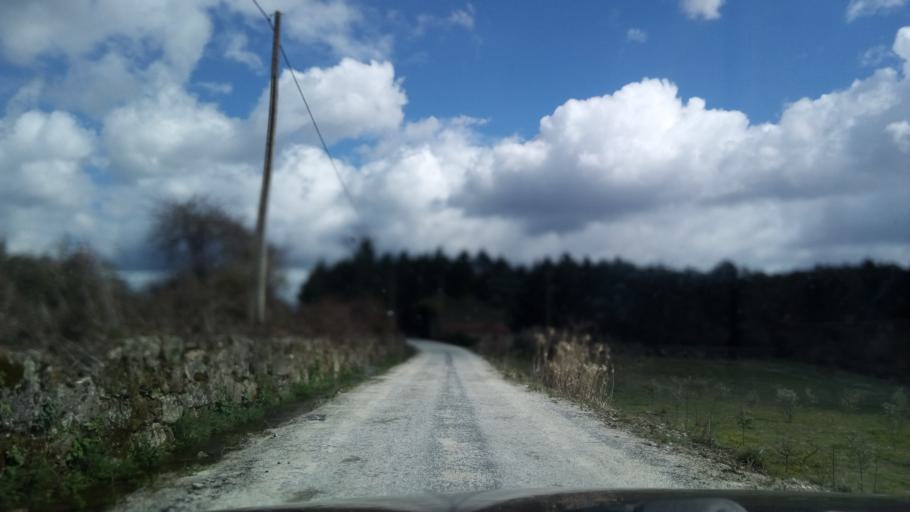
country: PT
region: Guarda
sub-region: Fornos de Algodres
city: Fornos de Algodres
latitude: 40.6320
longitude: -7.5201
